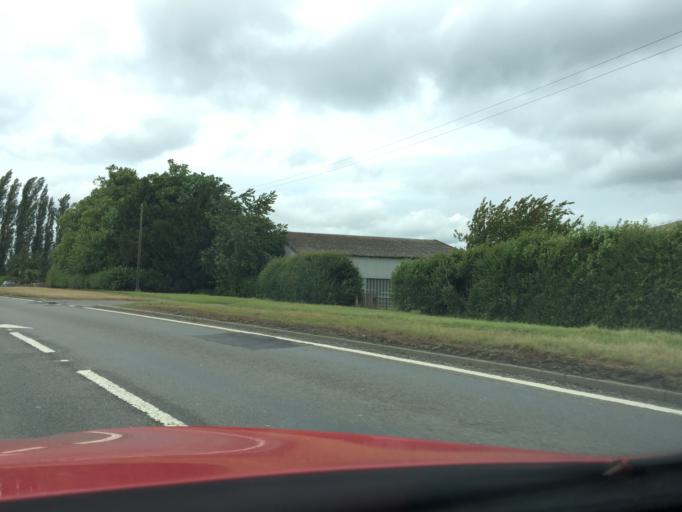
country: GB
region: England
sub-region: Northamptonshire
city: Long Buckby
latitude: 52.2357
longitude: -1.0929
